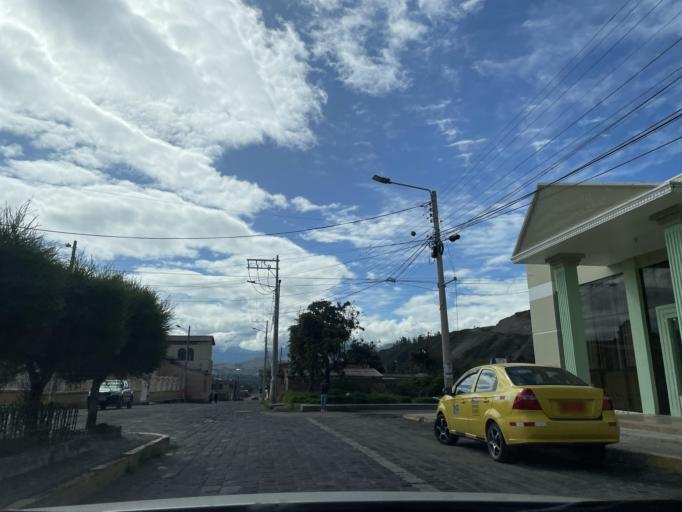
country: EC
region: Chimborazo
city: Guano
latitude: -1.6086
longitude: -78.6352
